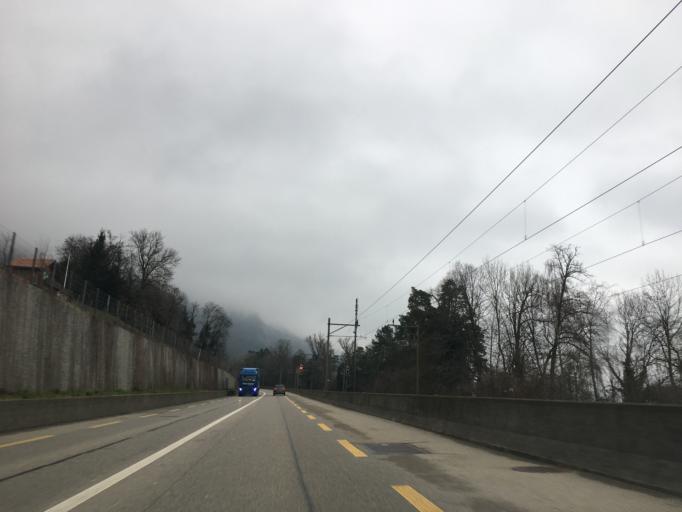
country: CH
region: Bern
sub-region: Jura bernois
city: La Neuveville
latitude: 47.0691
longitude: 7.1103
